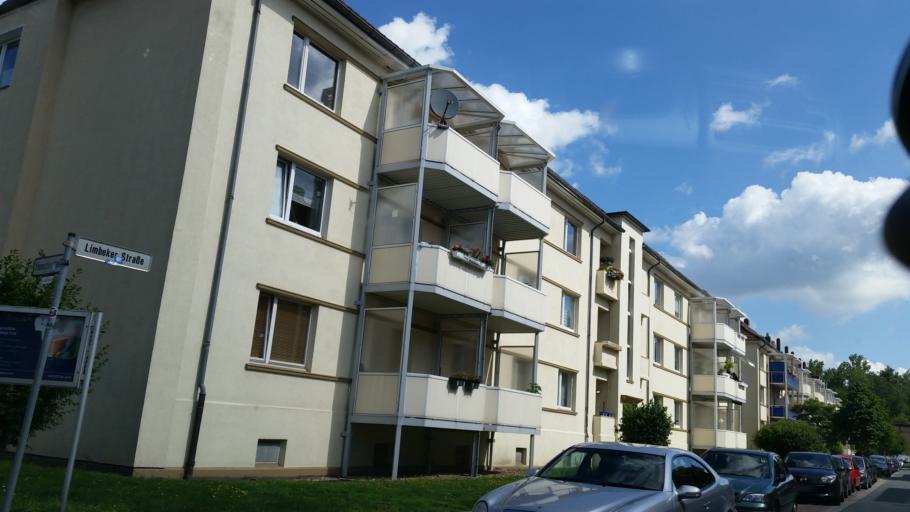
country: DE
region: Lower Saxony
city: Braunschweig
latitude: 52.2446
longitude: 10.5399
